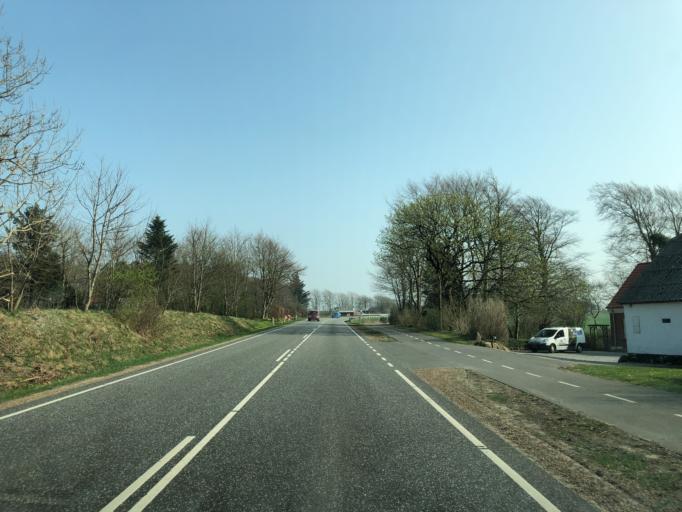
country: DK
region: Central Jutland
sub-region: Ringkobing-Skjern Kommune
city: Videbaek
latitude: 56.1087
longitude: 8.5059
